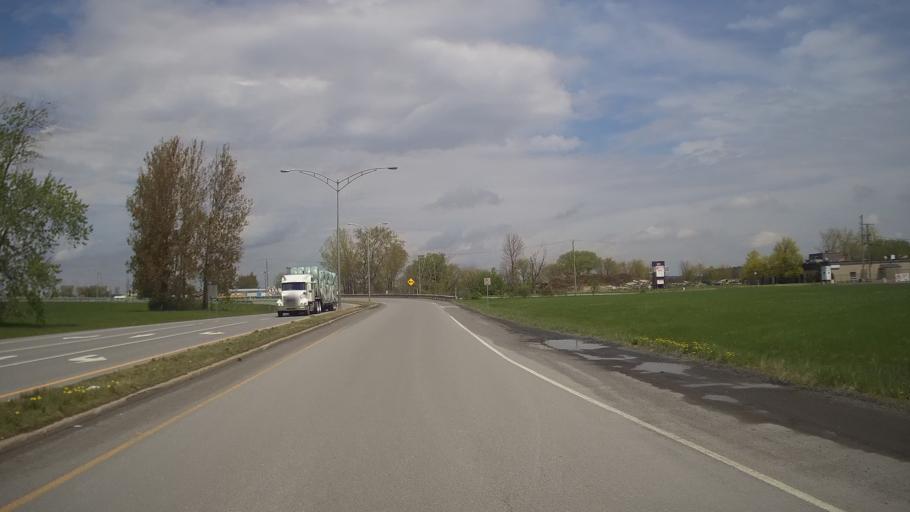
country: CA
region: Quebec
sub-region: Monteregie
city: Saint-Jean-sur-Richelieu
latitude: 45.3128
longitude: -73.2203
